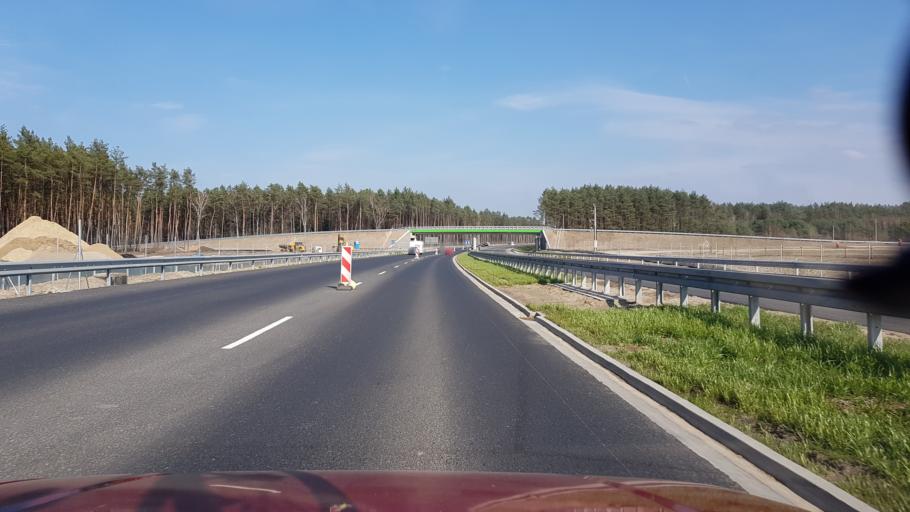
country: PL
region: West Pomeranian Voivodeship
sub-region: Powiat goleniowski
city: Mosty
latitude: 53.6111
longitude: 14.9036
